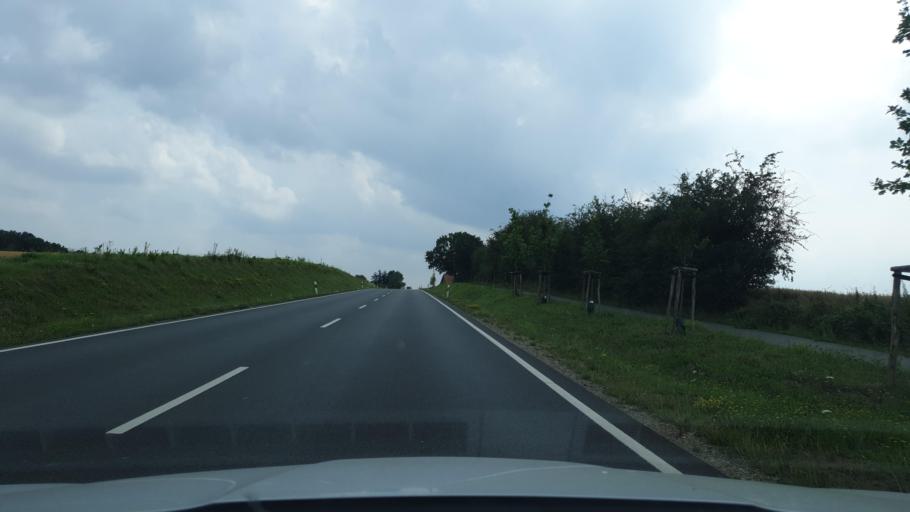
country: DE
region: North Rhine-Westphalia
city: Loehne
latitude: 52.1706
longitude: 8.7493
